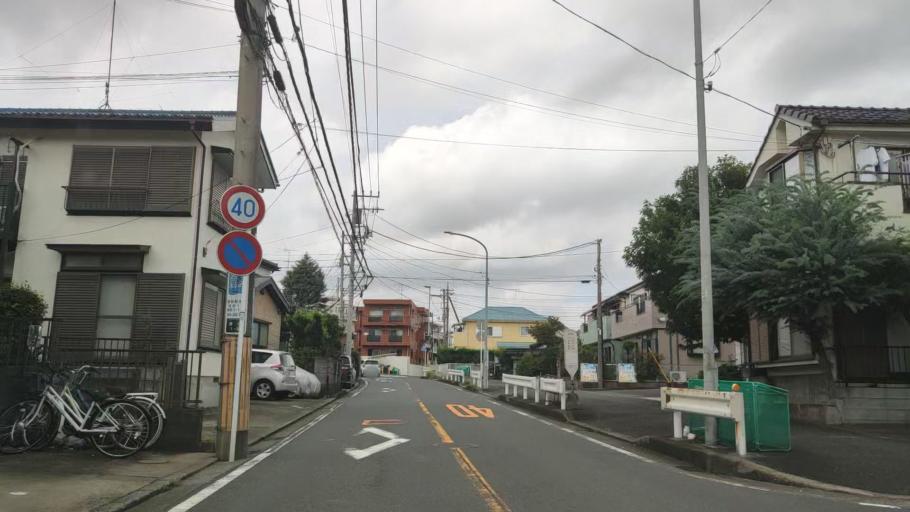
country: JP
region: Kanagawa
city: Minami-rinkan
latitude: 35.4693
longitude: 139.4923
